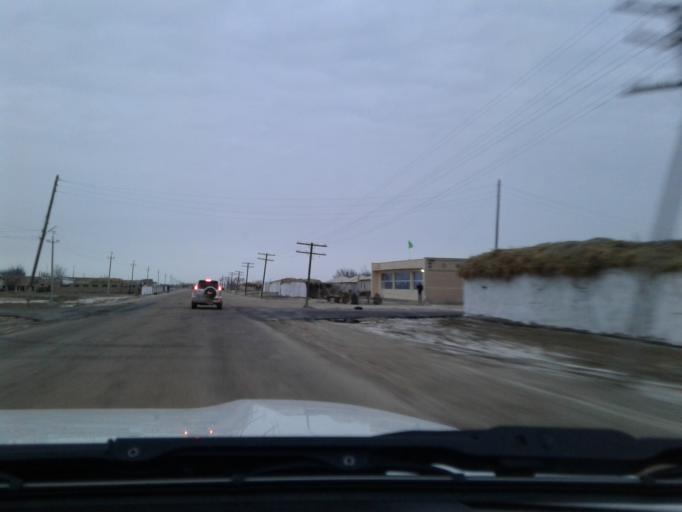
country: TM
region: Dasoguz
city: Dasoguz
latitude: 42.0111
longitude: 59.8878
